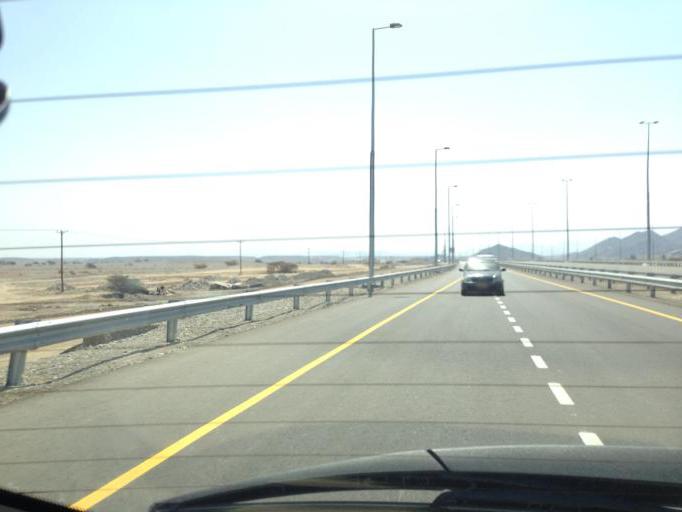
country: OM
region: Al Batinah
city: Rustaq
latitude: 23.5667
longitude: 57.4938
